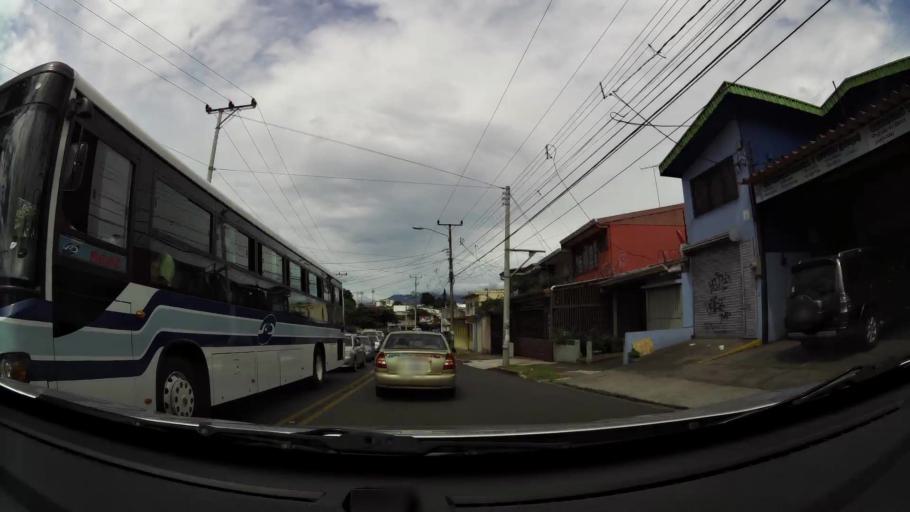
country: CR
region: San Jose
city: San Jose
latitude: 9.9180
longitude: -84.0752
